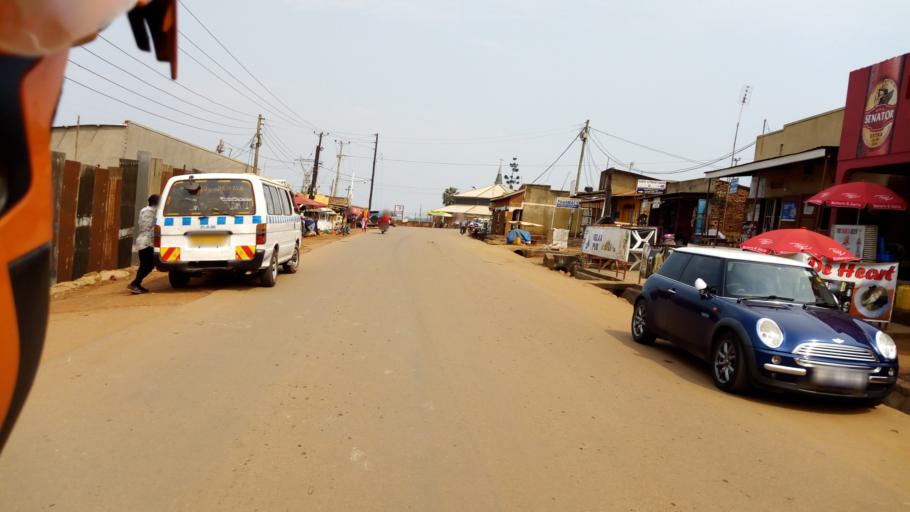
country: UG
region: Central Region
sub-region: Wakiso District
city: Kireka
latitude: 0.3108
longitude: 32.6520
